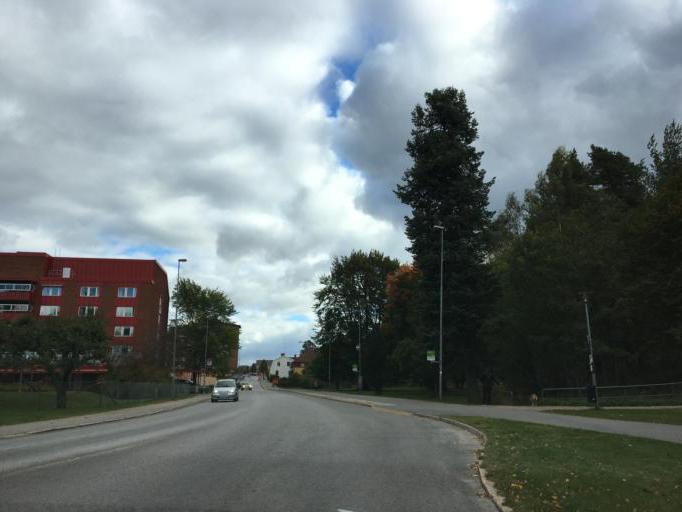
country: SE
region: Soedermanland
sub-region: Katrineholms Kommun
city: Katrineholm
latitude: 58.9916
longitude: 16.2036
